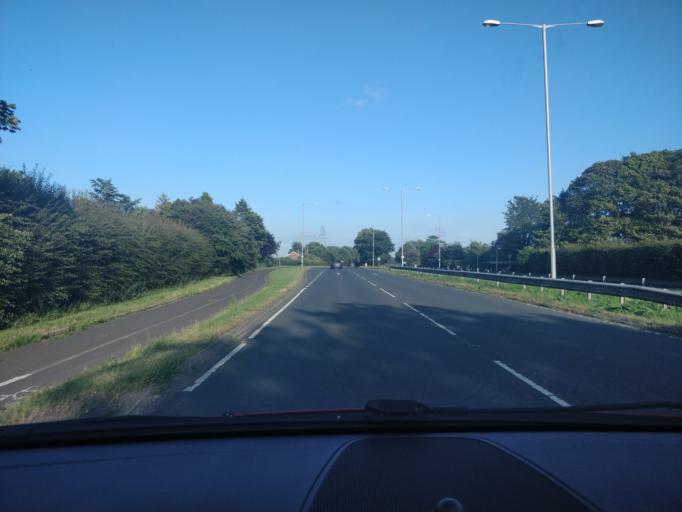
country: GB
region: England
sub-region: Lancashire
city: Banks
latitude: 53.6697
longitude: -2.9079
